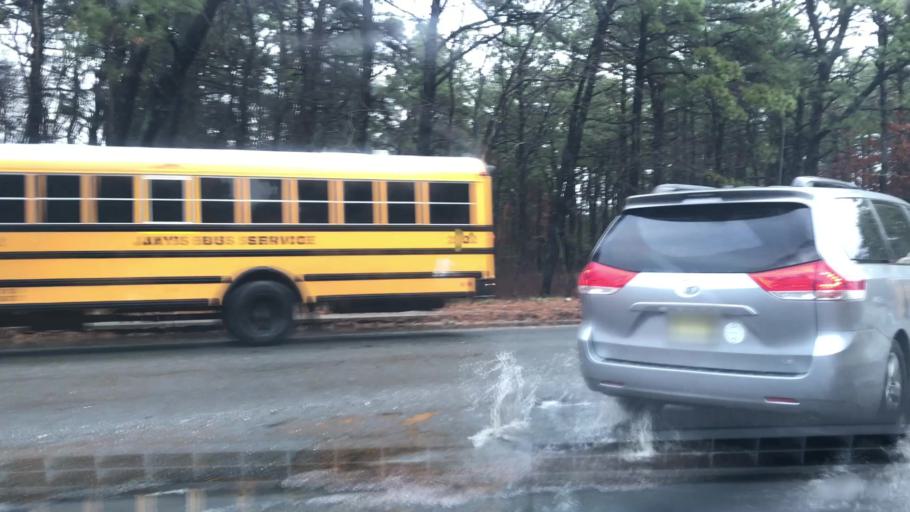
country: US
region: New Jersey
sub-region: Ocean County
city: Lakewood
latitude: 40.0753
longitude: -74.2062
